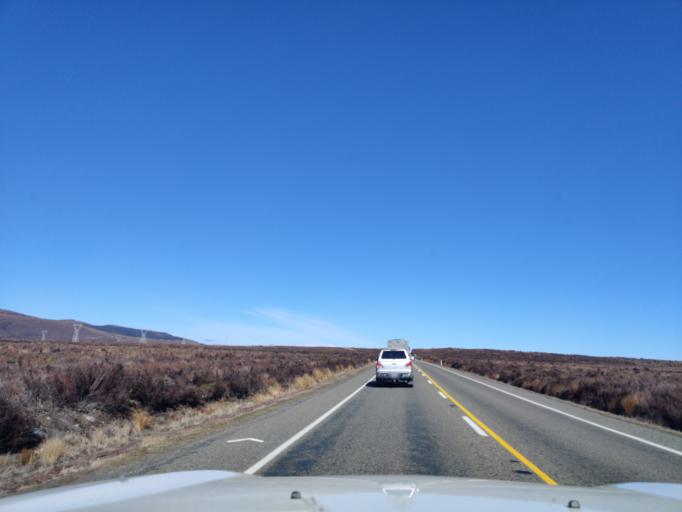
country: NZ
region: Manawatu-Wanganui
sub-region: Ruapehu District
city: Waiouru
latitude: -39.2570
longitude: 175.7352
